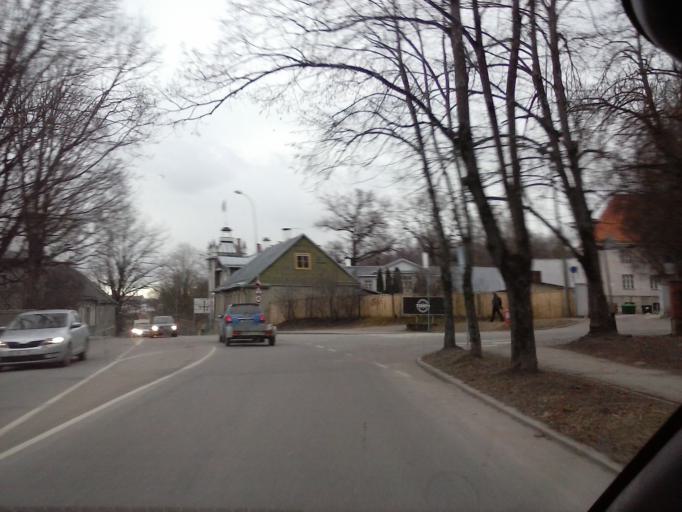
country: EE
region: Tartu
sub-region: Tartu linn
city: Tartu
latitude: 58.3831
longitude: 26.7106
